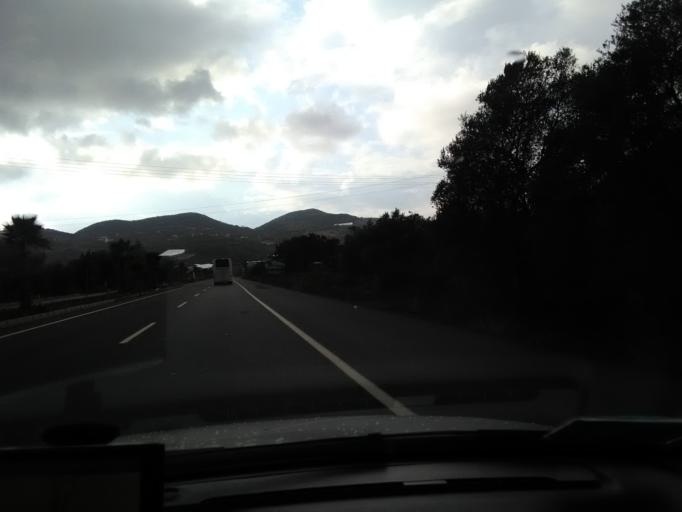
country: TR
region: Antalya
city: Gazipasa
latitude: 36.1925
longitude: 32.4155
